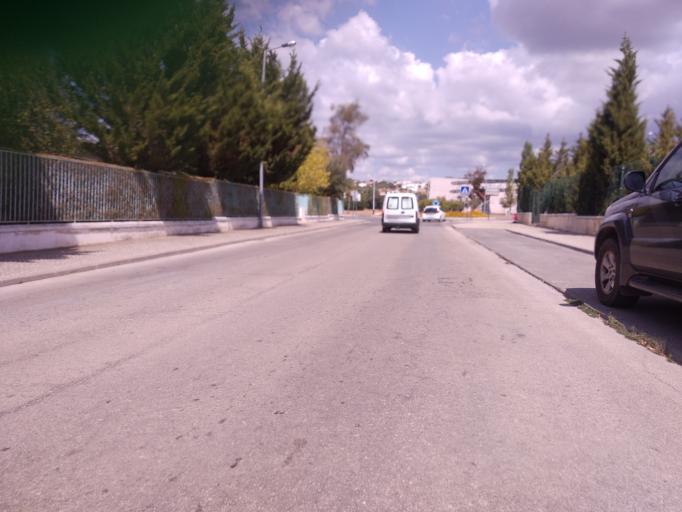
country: PT
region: Faro
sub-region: Sao Bras de Alportel
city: Sao Bras de Alportel
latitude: 37.1558
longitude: -7.8830
